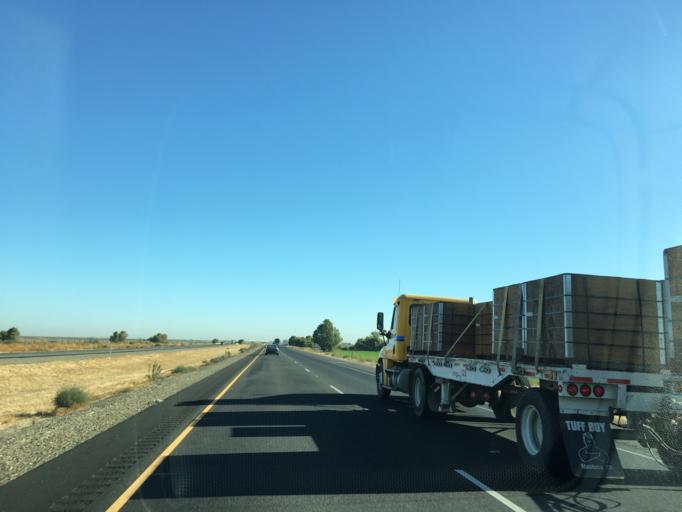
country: US
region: California
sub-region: Merced County
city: Dos Palos
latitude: 37.0584
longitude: -120.5464
